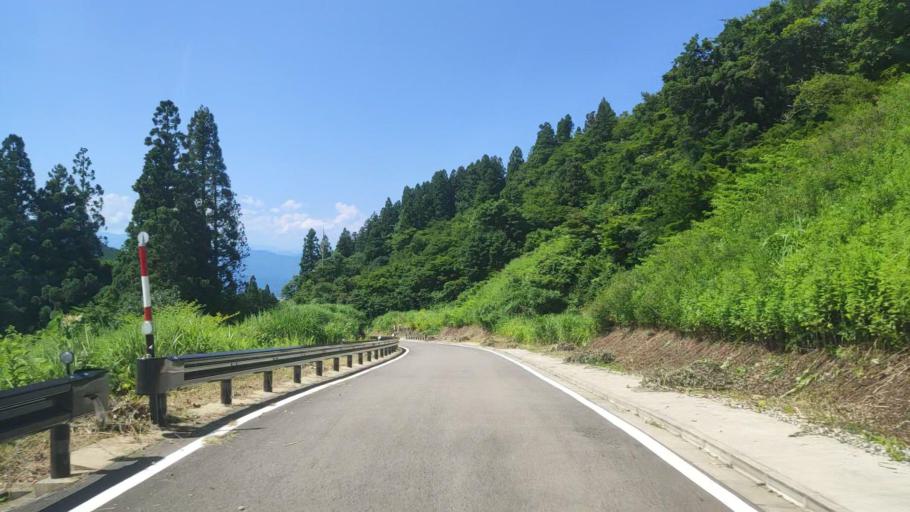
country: JP
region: Fukui
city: Katsuyama
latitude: 36.1417
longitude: 136.5192
